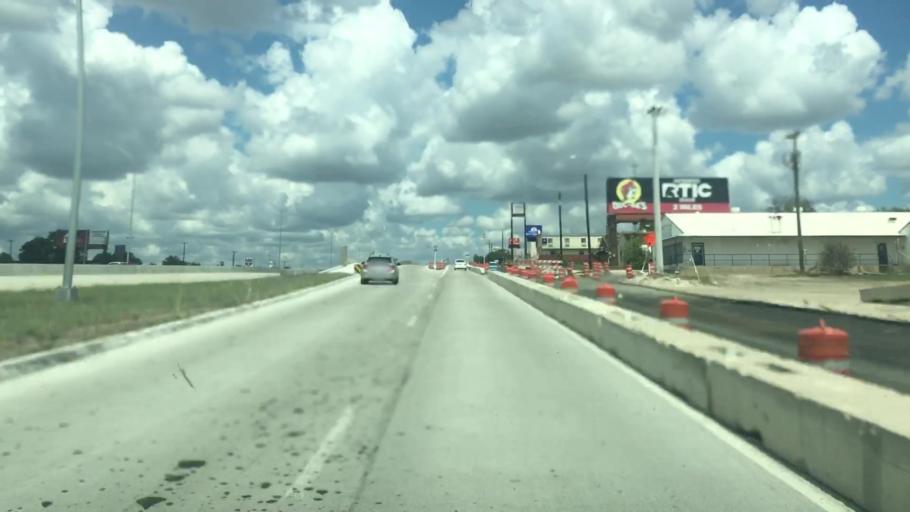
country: US
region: Texas
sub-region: Bell County
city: Temple
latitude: 31.1087
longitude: -97.3569
